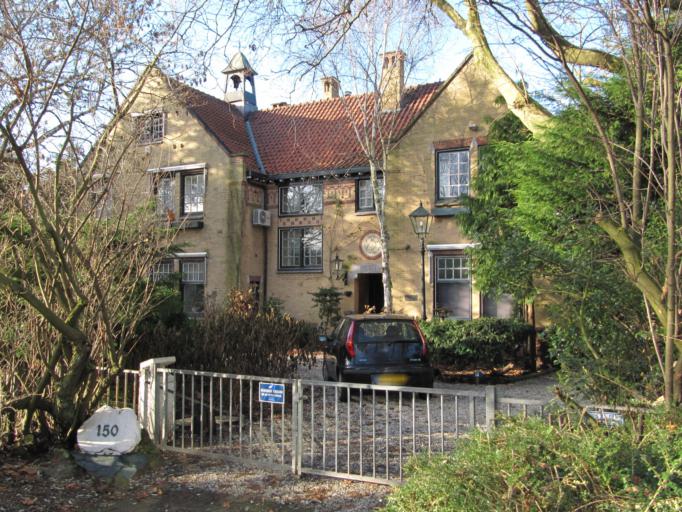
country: NL
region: South Holland
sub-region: Gemeente Rijswijk
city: Rijswijk
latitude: 52.0463
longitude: 4.3159
